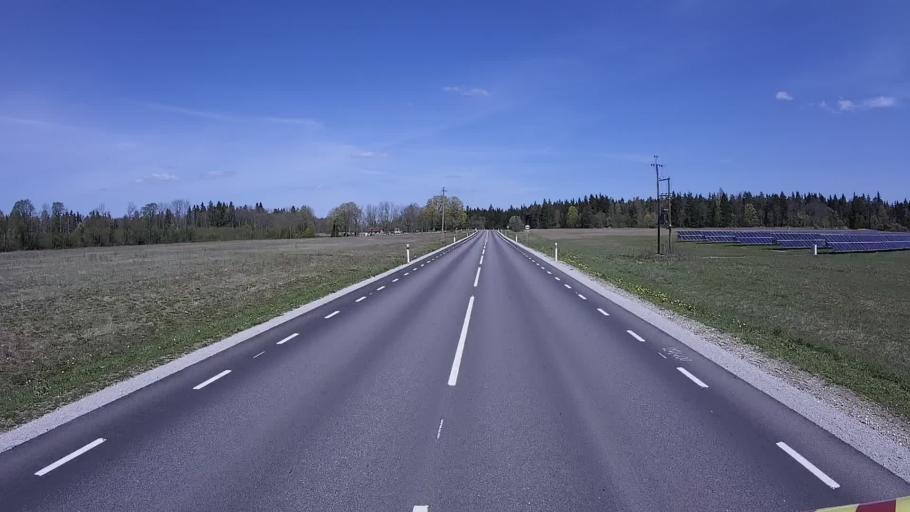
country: EE
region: Harju
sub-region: Paldiski linn
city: Paldiski
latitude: 59.1957
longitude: 24.0951
